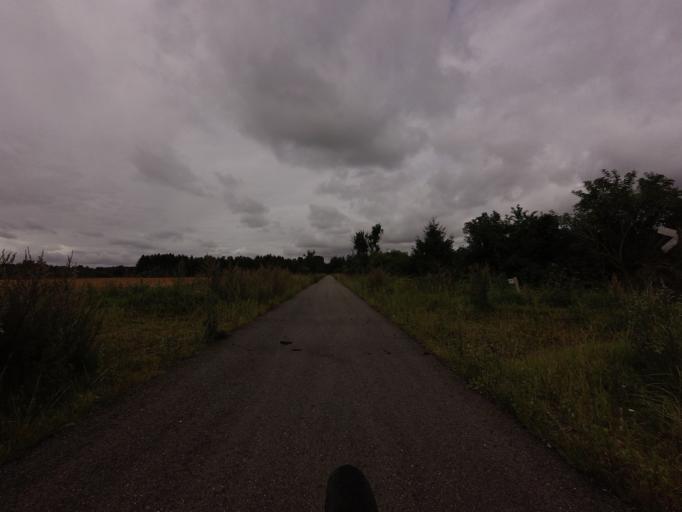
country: DK
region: Central Jutland
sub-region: Syddjurs Kommune
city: Ryomgard
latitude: 56.3851
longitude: 10.4589
